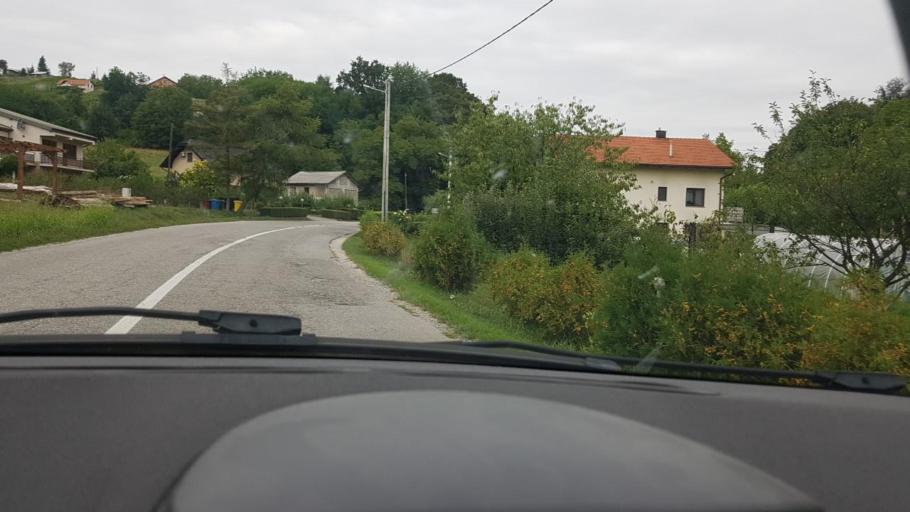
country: SI
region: Rogatec
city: Rogatec
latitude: 46.2012
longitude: 15.6949
